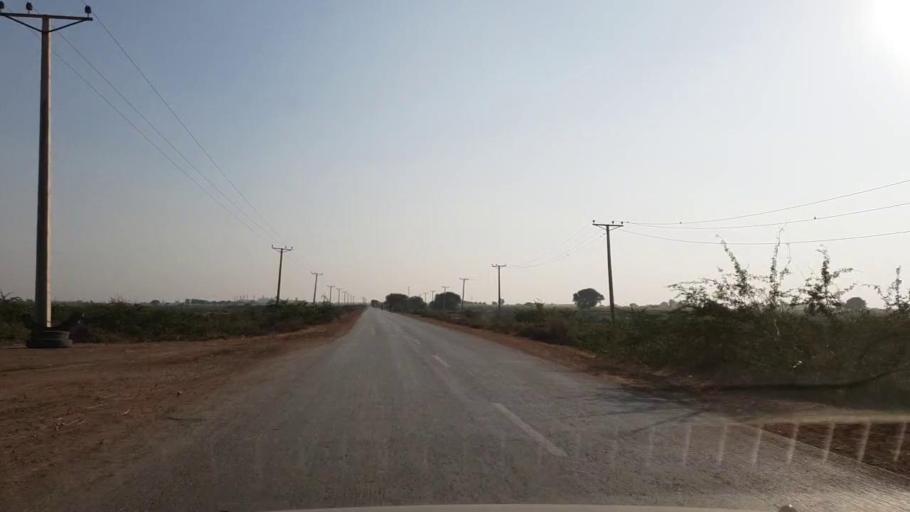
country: PK
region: Sindh
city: Bulri
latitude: 24.8281
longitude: 68.3227
